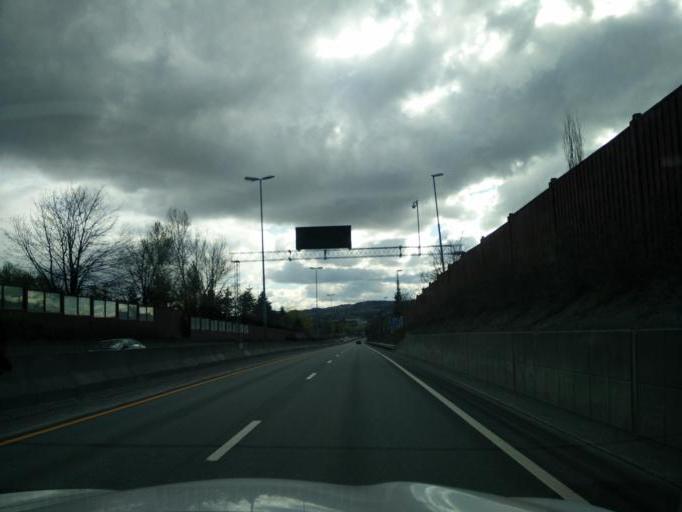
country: NO
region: Sor-Trondelag
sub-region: Trondheim
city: Trondheim
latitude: 63.4053
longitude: 10.4158
